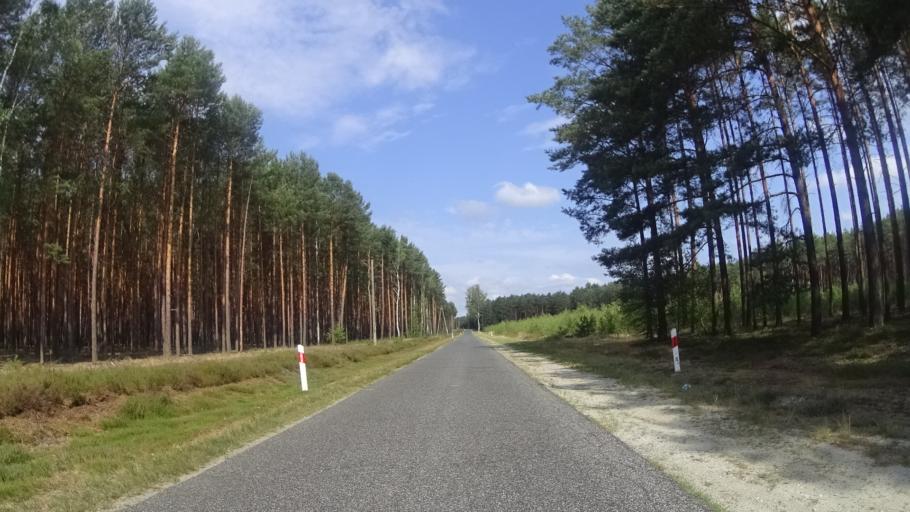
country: PL
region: Lubusz
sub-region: Powiat zarski
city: Leknica
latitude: 51.5160
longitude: 14.8308
